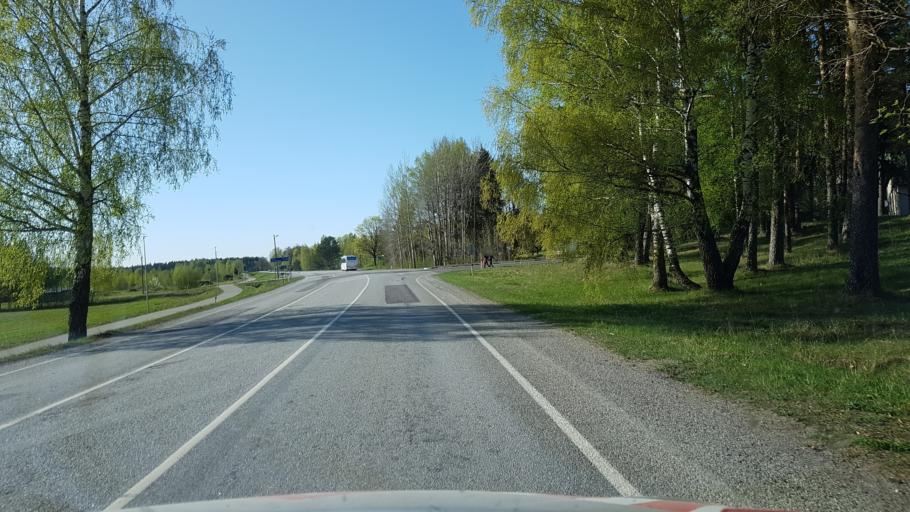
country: EE
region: Paernumaa
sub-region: Paikuse vald
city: Paikuse
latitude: 58.3570
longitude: 24.6613
